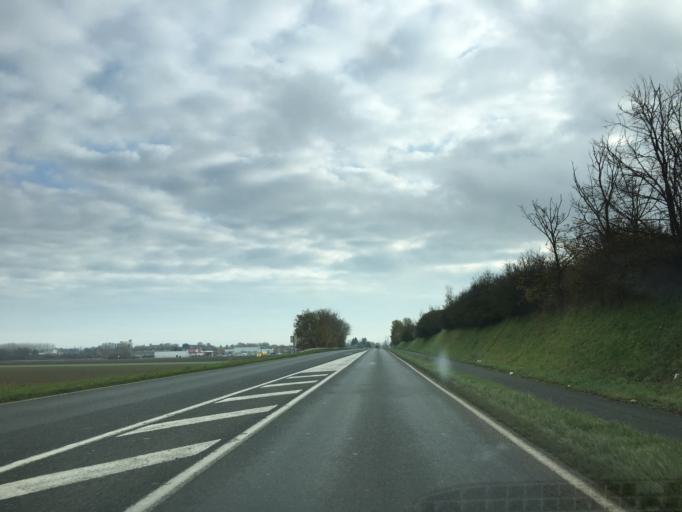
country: FR
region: Bourgogne
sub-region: Departement de l'Yonne
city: Pont-sur-Yonne
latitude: 48.2974
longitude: 3.1889
